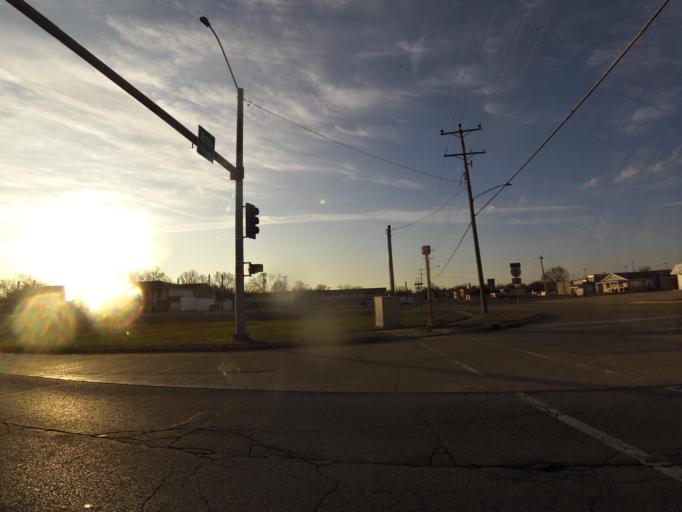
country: US
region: Illinois
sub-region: Fayette County
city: Vandalia
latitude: 38.9773
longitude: -89.1000
